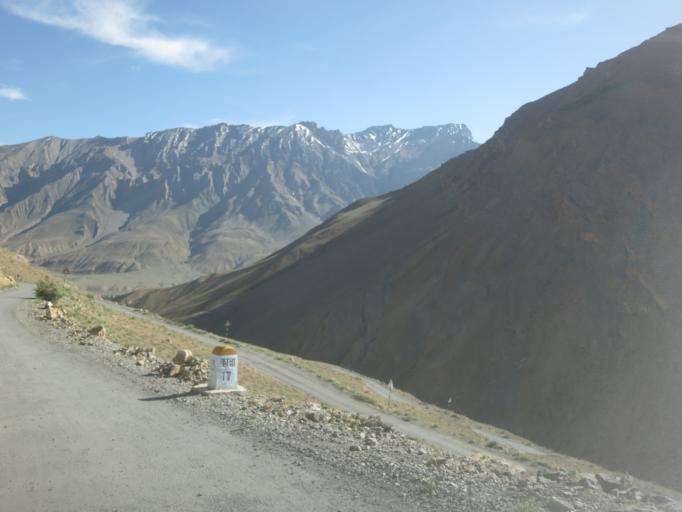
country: IN
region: Himachal Pradesh
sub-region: Kulu
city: Manali
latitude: 32.3244
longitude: 78.0021
